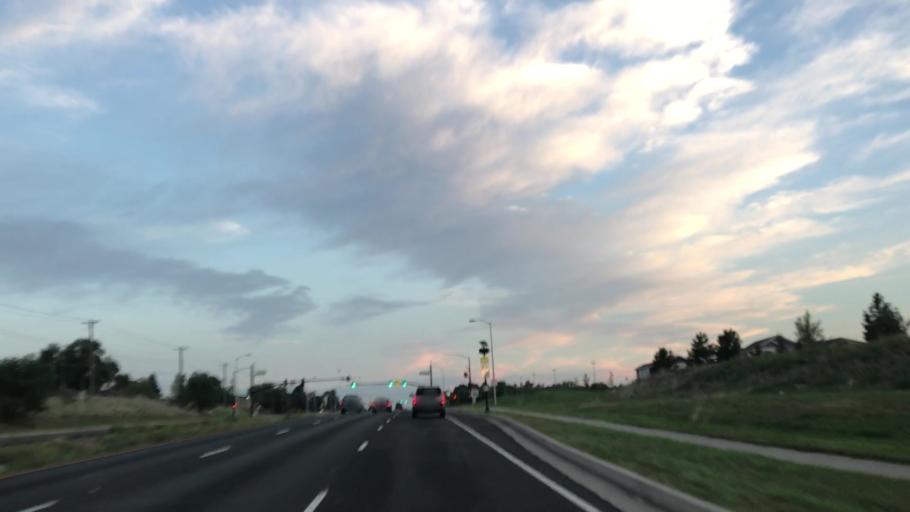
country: US
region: Colorado
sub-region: El Paso County
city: Stratmoor
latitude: 38.8123
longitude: -104.7803
